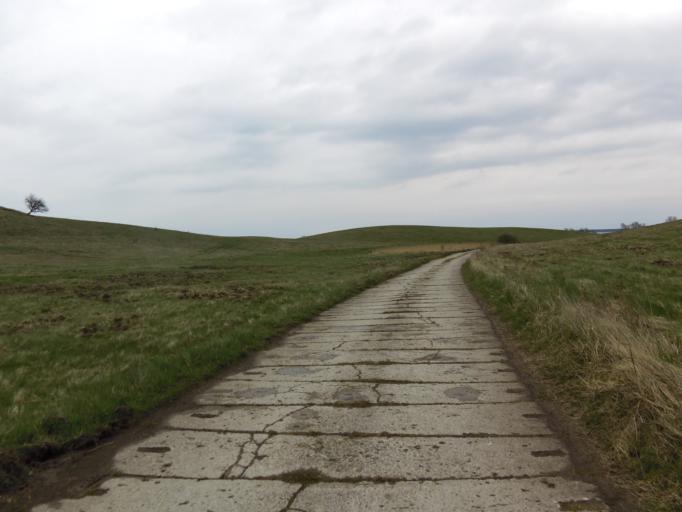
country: DE
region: Mecklenburg-Vorpommern
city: Hiddensee
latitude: 54.5998
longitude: 13.1297
